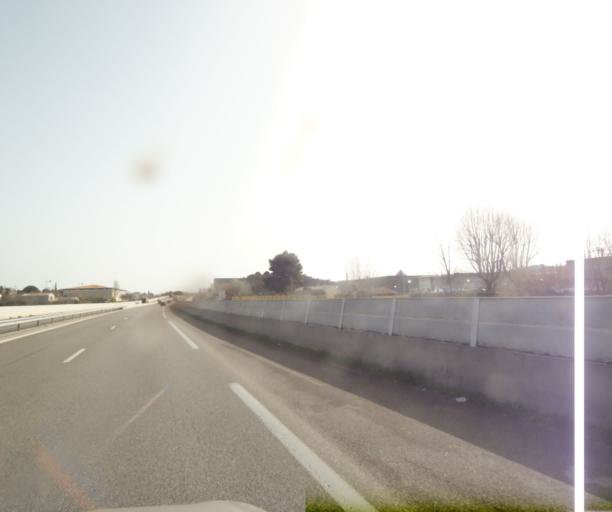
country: FR
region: Provence-Alpes-Cote d'Azur
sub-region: Departement des Bouches-du-Rhone
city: Meyreuil
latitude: 43.4727
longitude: 5.4910
